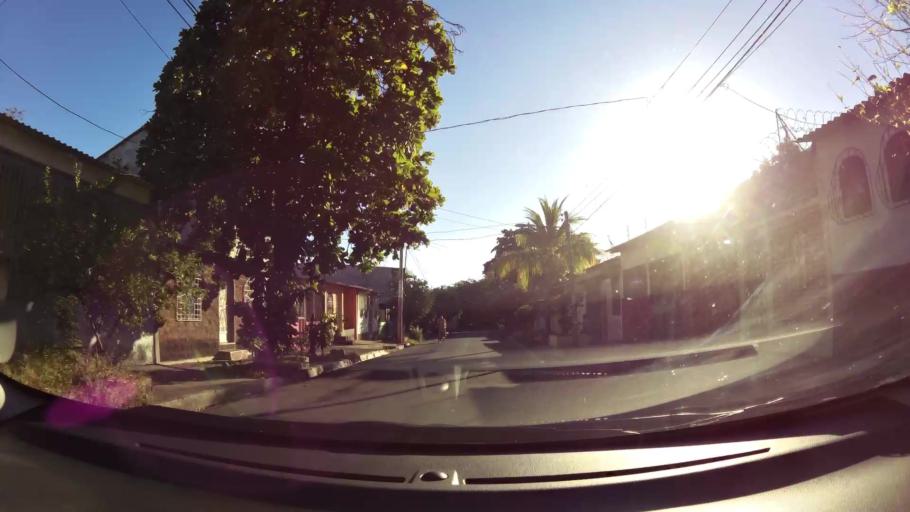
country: SV
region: San Miguel
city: San Miguel
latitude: 13.4877
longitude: -88.1673
